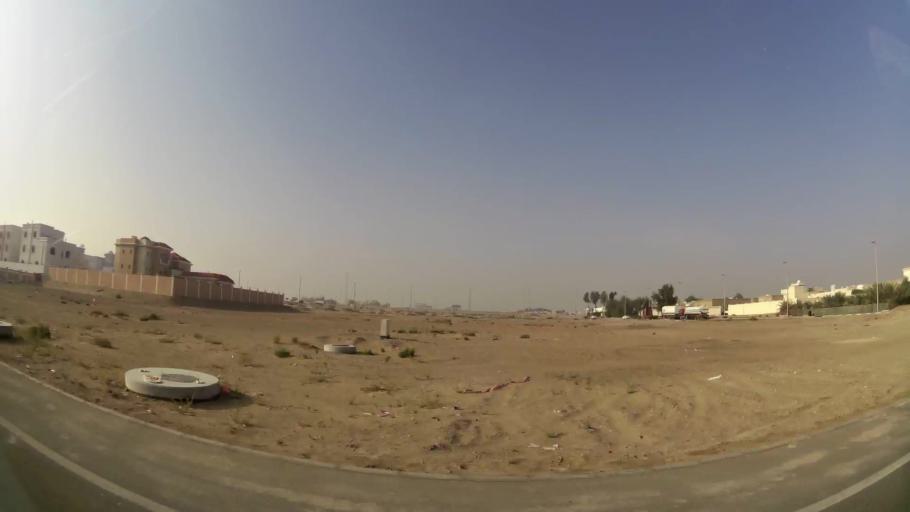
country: AE
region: Abu Dhabi
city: Abu Dhabi
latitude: 24.2748
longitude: 54.6501
